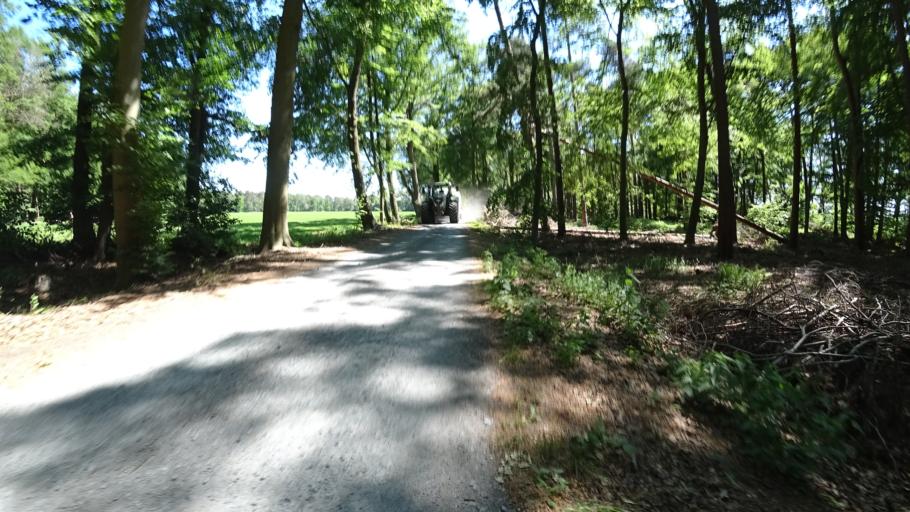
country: DE
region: North Rhine-Westphalia
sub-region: Regierungsbezirk Detmold
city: Guetersloh
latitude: 51.8649
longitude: 8.3528
